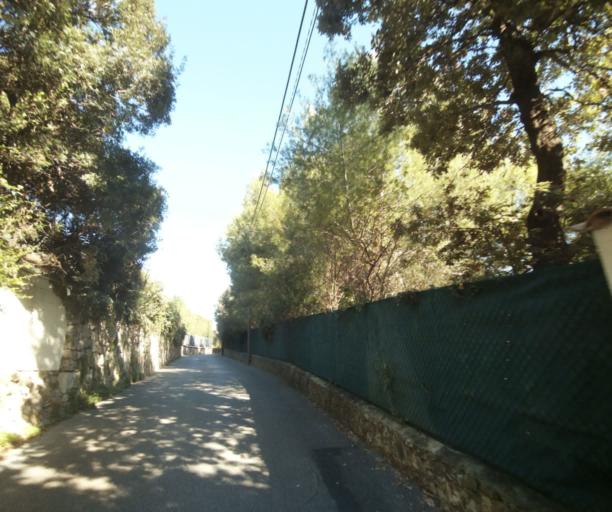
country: FR
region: Provence-Alpes-Cote d'Azur
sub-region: Departement des Alpes-Maritimes
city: Antibes
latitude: 43.5627
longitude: 7.1228
